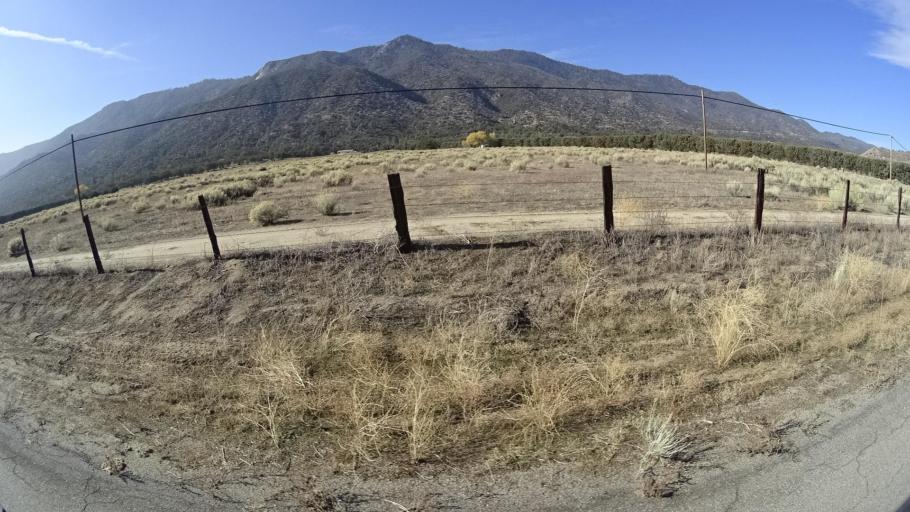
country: US
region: California
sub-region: Kern County
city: Bodfish
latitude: 35.4267
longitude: -118.5356
